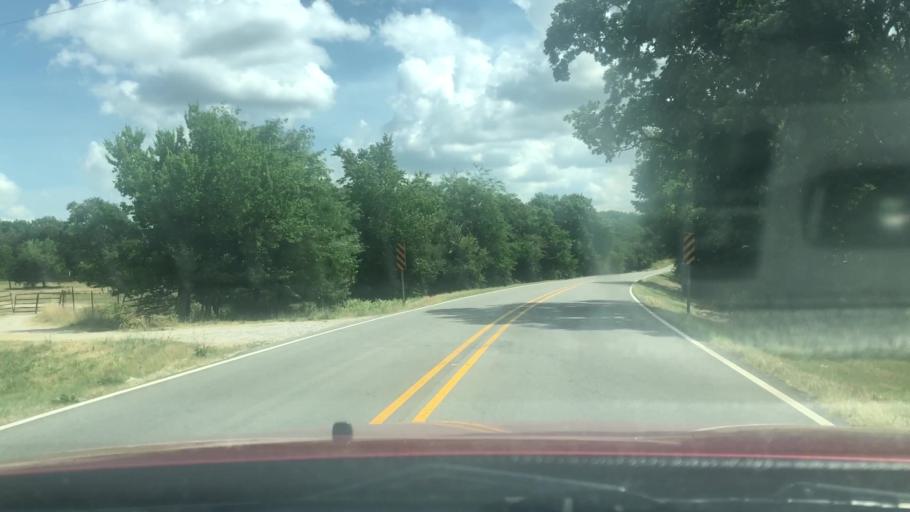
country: US
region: Arkansas
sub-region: Carroll County
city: Berryville
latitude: 36.4086
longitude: -93.5398
